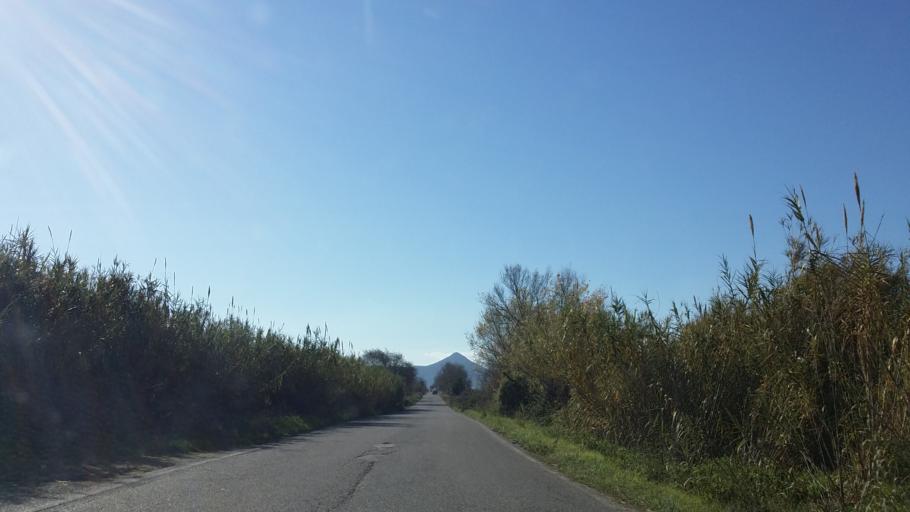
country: GR
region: West Greece
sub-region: Nomos Aitolias kai Akarnanias
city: Vonitsa
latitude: 38.8597
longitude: 20.8773
